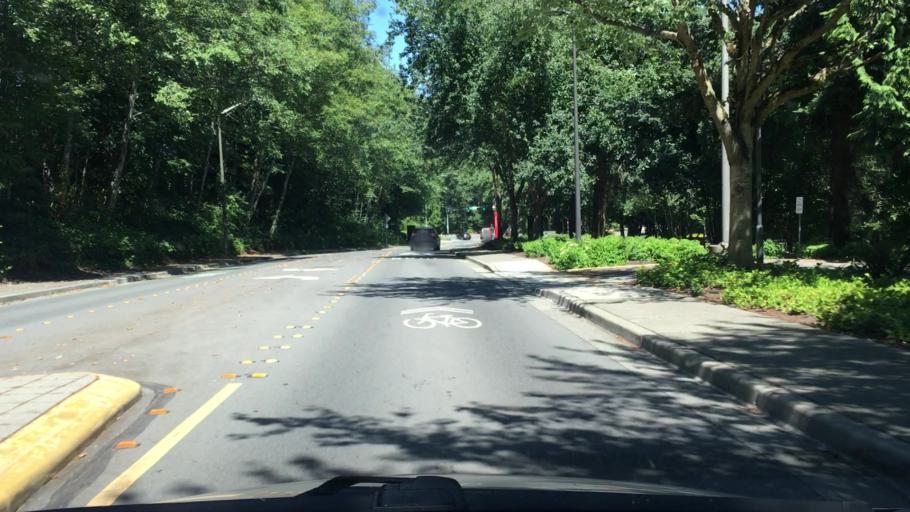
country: US
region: Washington
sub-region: King County
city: Redmond
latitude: 47.6442
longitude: -122.1232
